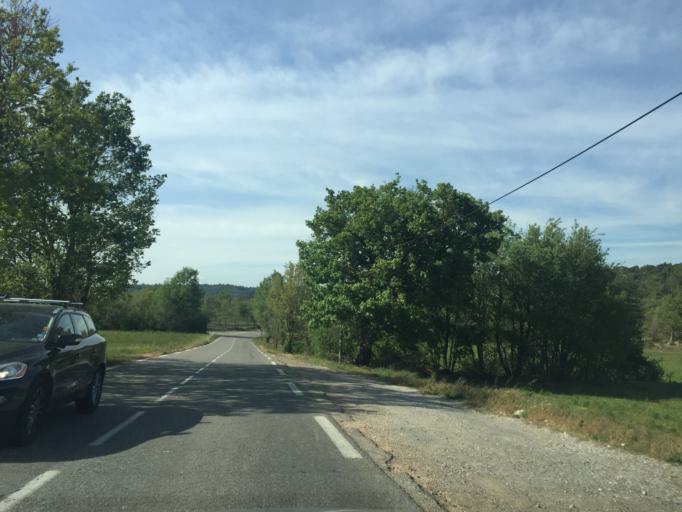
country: FR
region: Provence-Alpes-Cote d'Azur
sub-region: Departement du Var
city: Ginasservis
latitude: 43.6896
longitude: 5.8371
